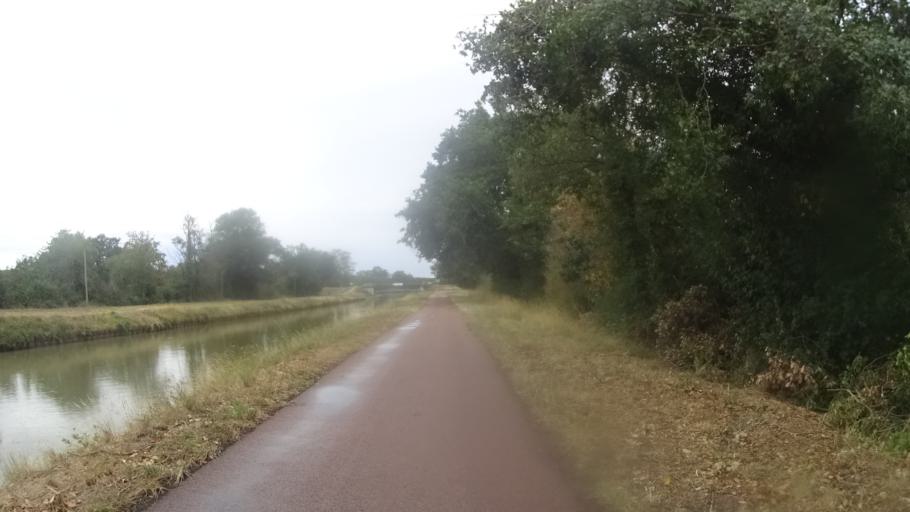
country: FR
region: Bourgogne
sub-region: Departement de la Nievre
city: Imphy
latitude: 46.8719
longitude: 3.2727
